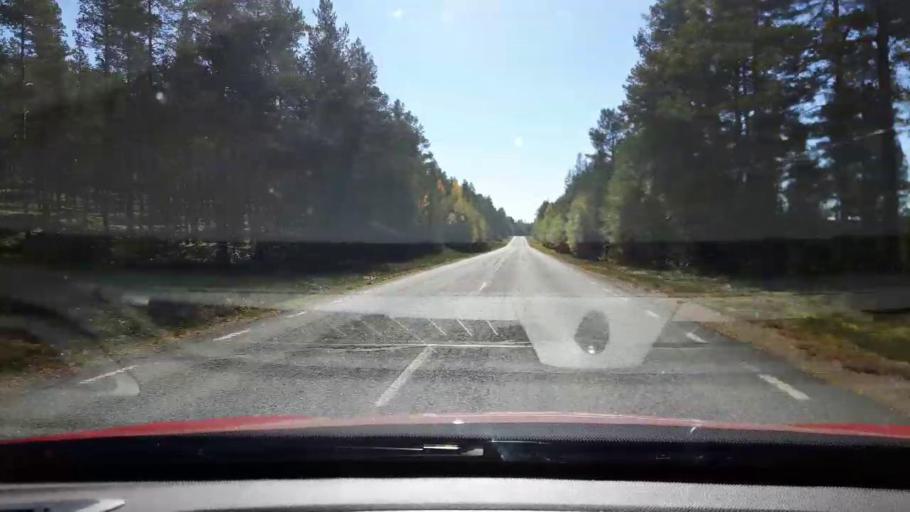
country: SE
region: Jaemtland
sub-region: Harjedalens Kommun
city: Sveg
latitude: 62.3309
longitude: 14.0570
